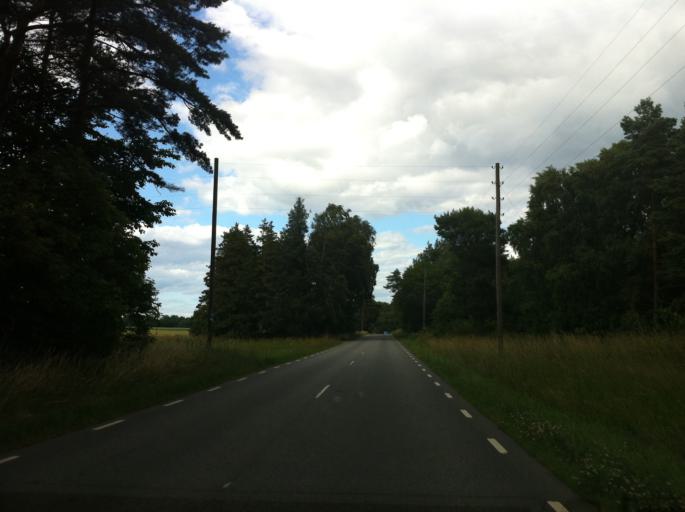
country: SE
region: Skane
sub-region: Simrishamns Kommun
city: Simrishamn
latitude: 55.4247
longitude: 14.2163
